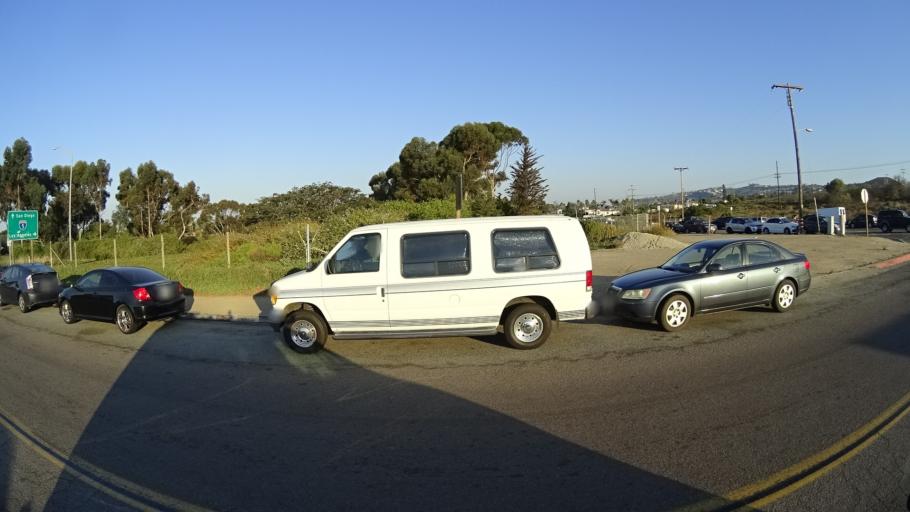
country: US
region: California
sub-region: Orange County
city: San Clemente
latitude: 33.3958
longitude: -117.5919
